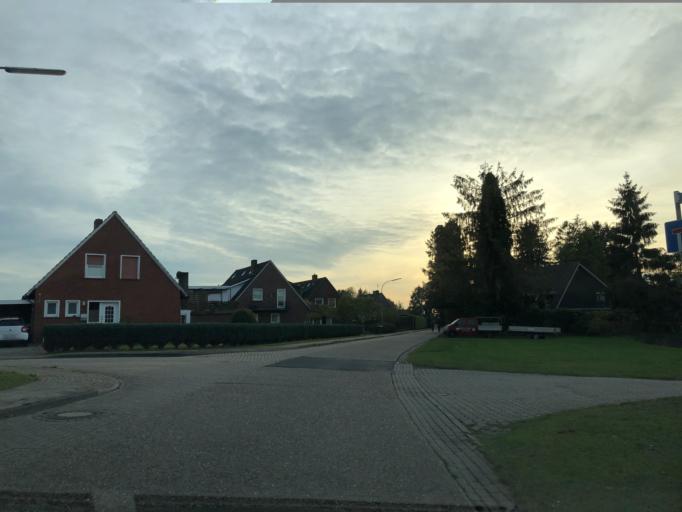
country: DE
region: Lower Saxony
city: Lehe
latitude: 53.0457
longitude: 7.3299
